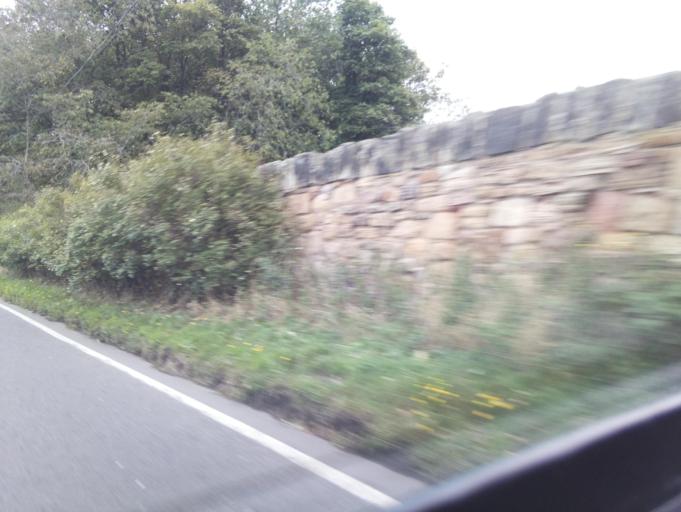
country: GB
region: Scotland
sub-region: East Lothian
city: Prestonpans
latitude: 55.9458
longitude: -3.0030
